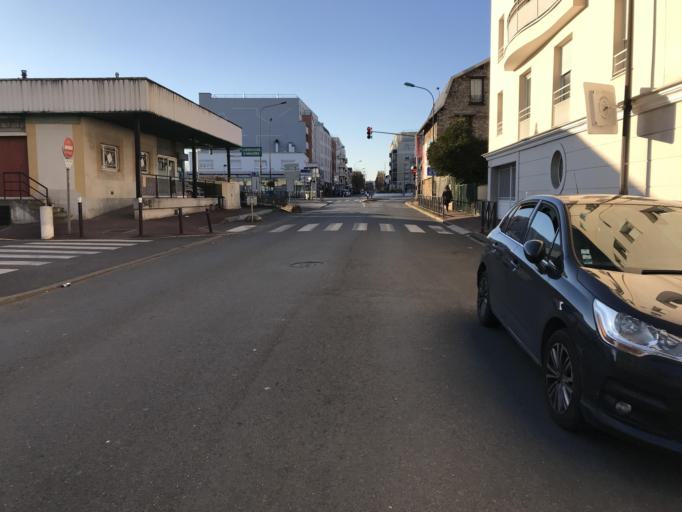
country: FR
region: Ile-de-France
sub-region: Departement de l'Essonne
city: Chilly-Mazarin
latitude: 48.7020
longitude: 2.3216
